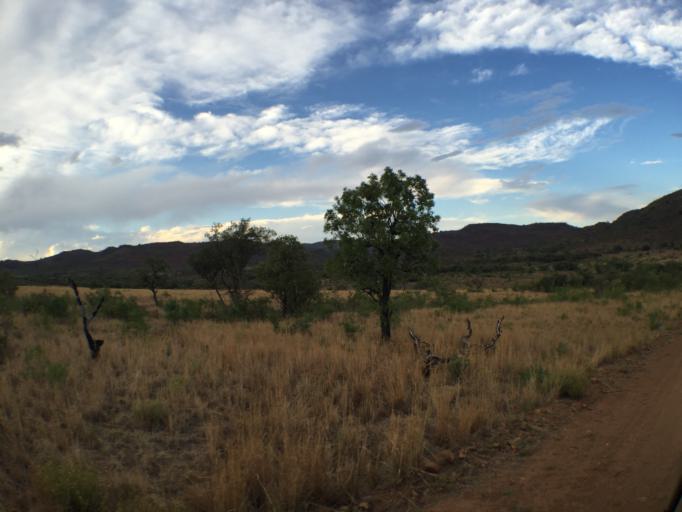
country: ZA
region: North-West
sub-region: Bojanala Platinum District Municipality
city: Mogwase
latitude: -25.2259
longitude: 27.0777
